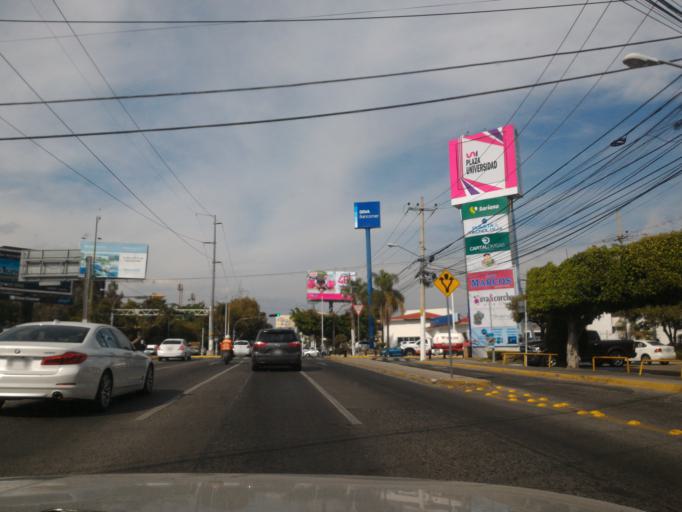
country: MX
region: Jalisco
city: Zapopan2
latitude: 20.6912
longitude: -103.4151
